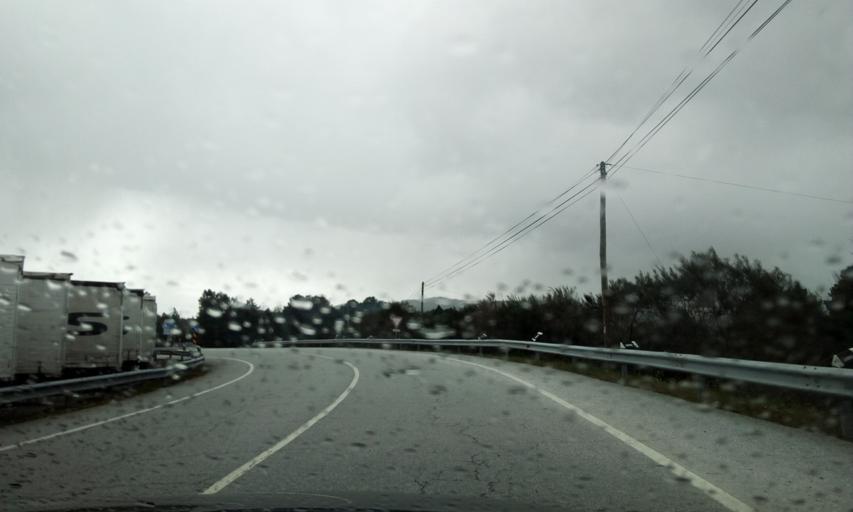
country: PT
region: Guarda
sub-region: Fornos de Algodres
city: Fornos de Algodres
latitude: 40.6187
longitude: -7.6143
